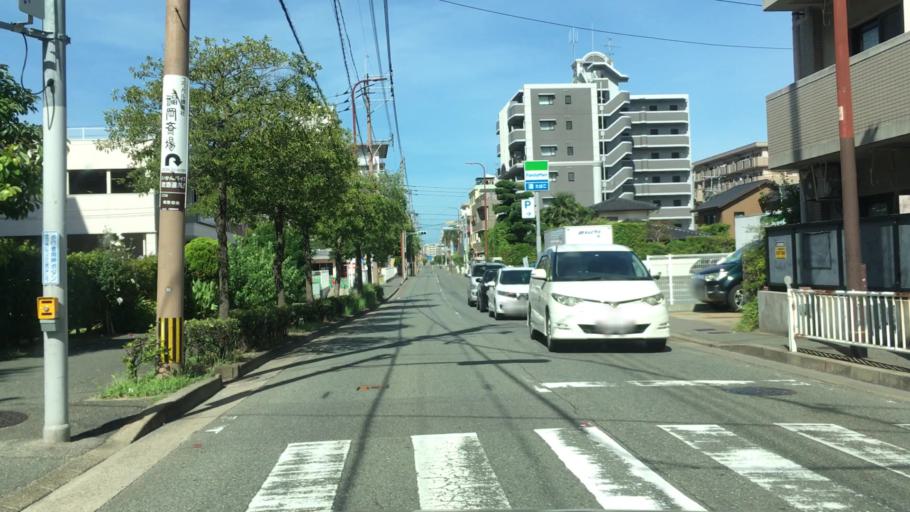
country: JP
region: Fukuoka
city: Fukuoka-shi
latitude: 33.5751
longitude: 130.3652
